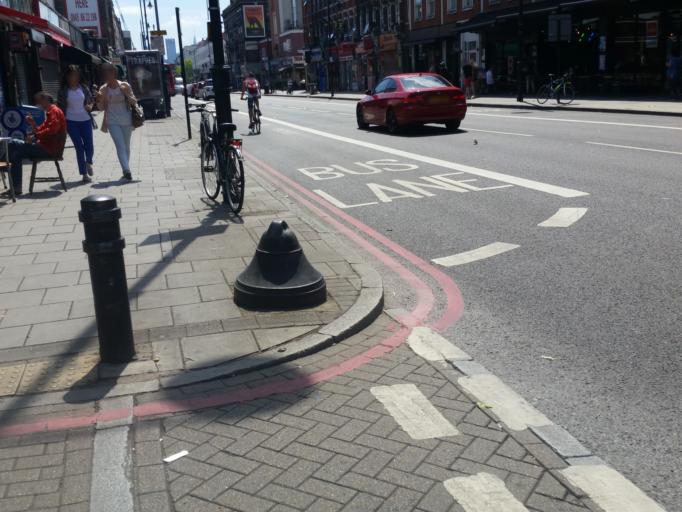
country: GB
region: England
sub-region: Greater London
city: Hackney
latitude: 51.5522
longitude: -0.0750
